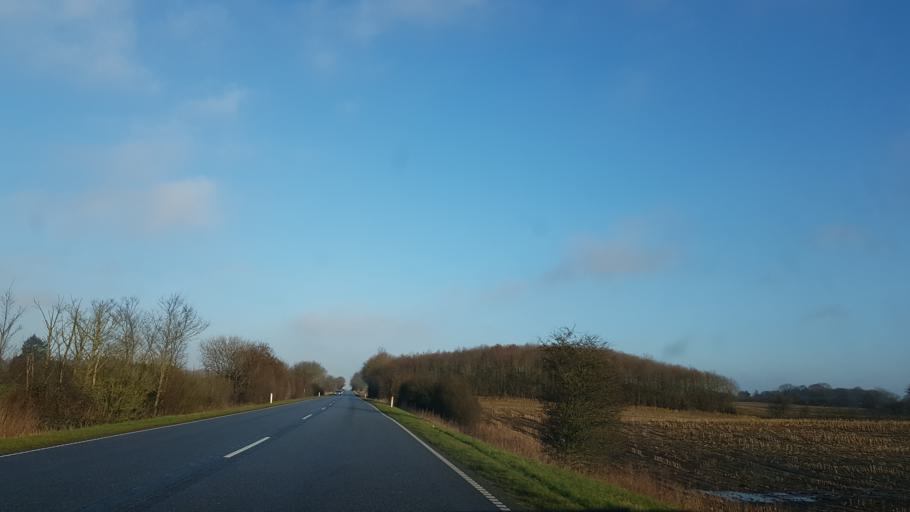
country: DK
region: South Denmark
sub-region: Haderslev Kommune
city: Vojens
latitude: 55.1737
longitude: 9.3868
